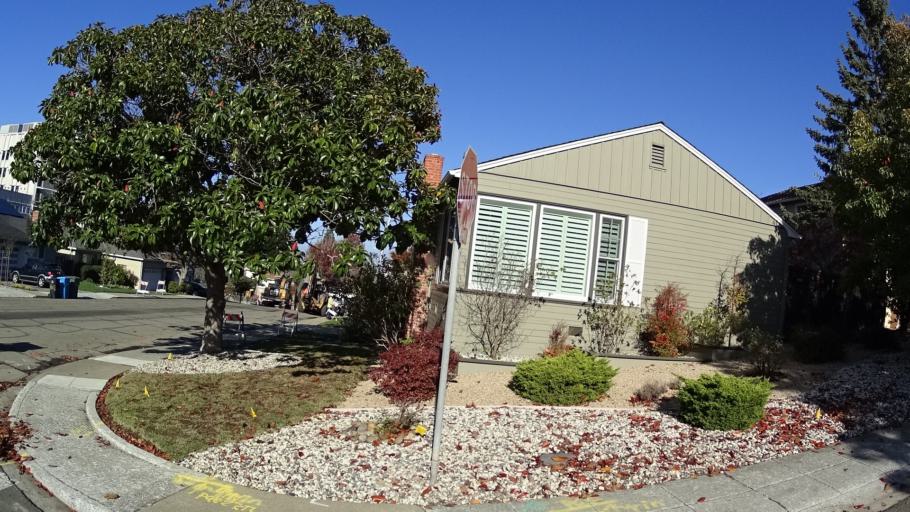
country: US
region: California
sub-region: San Mateo County
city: Millbrae
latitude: 37.5908
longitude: -122.3820
